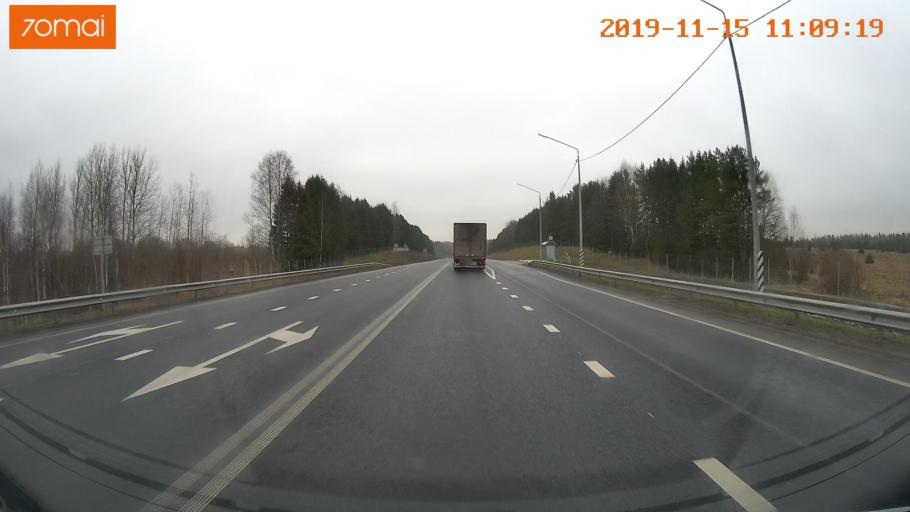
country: RU
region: Vologda
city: Chebsara
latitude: 59.1204
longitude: 39.0952
